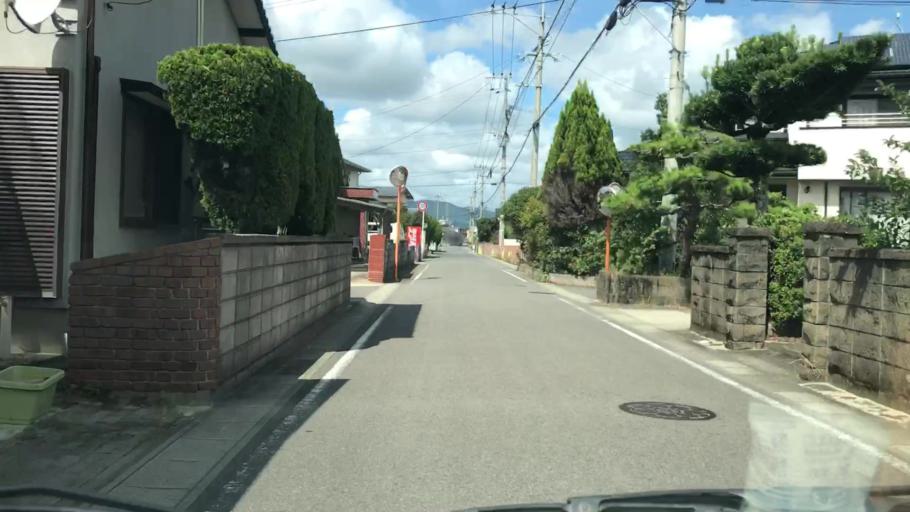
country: JP
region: Saga Prefecture
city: Saga-shi
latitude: 33.2417
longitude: 130.2016
